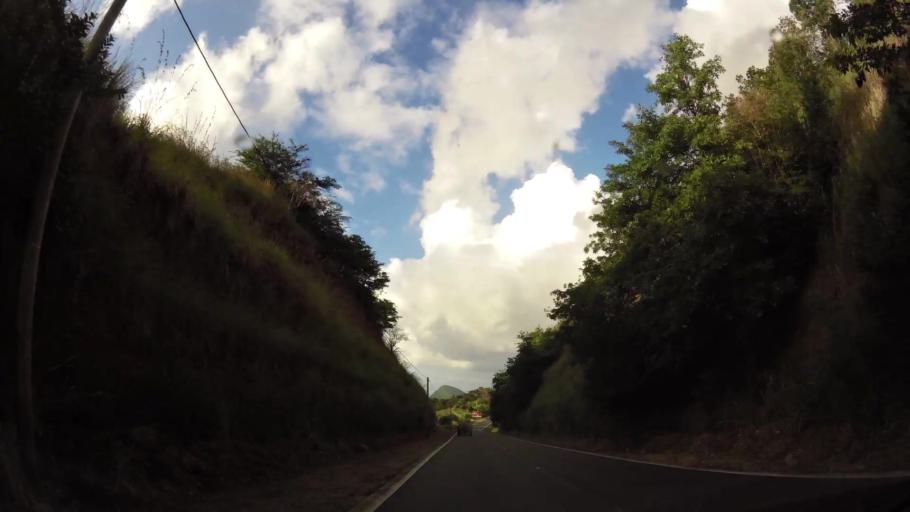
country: DM
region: Saint John
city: Portsmouth
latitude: 15.5421
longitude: -61.4746
